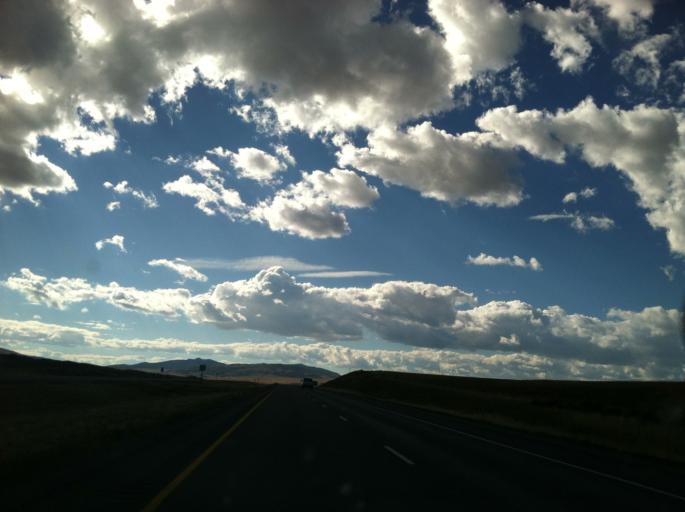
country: US
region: Montana
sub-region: Gallatin County
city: Three Forks
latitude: 45.9149
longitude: -111.7320
